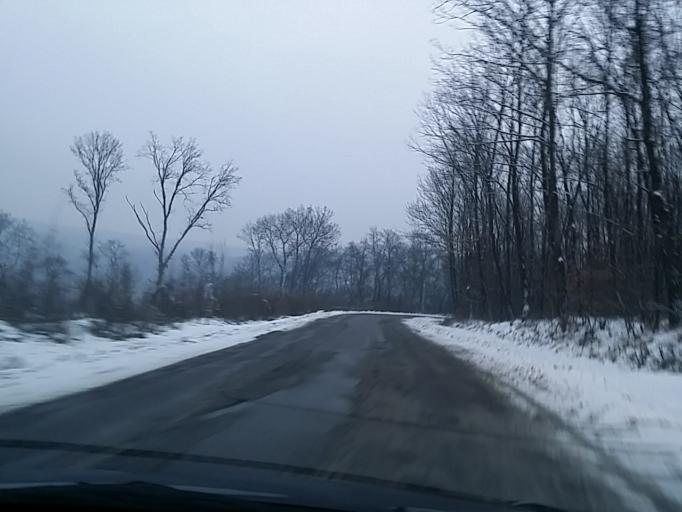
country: HU
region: Heves
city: Sirok
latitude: 47.8952
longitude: 20.1867
